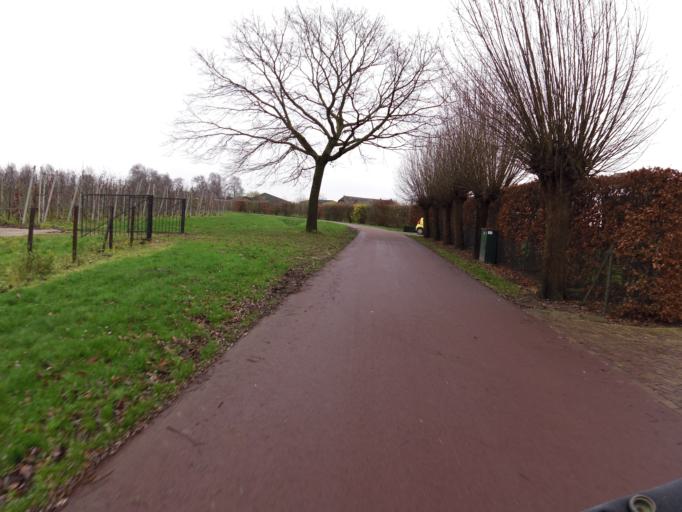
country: NL
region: Gelderland
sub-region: Gemeente Overbetuwe
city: Elst
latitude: 51.8891
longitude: 5.8687
